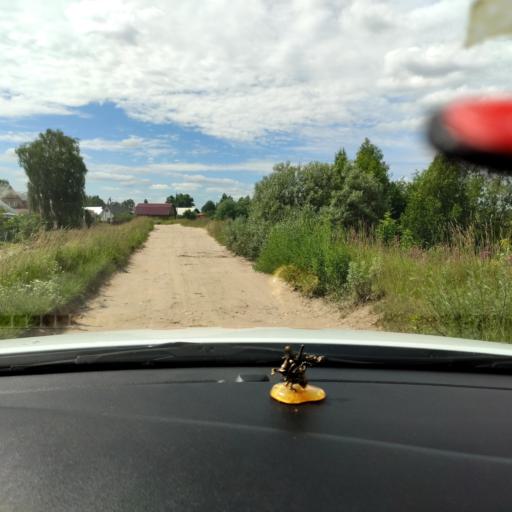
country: RU
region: Tatarstan
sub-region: Zelenodol'skiy Rayon
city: Vasil'yevo
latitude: 55.8363
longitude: 48.7190
